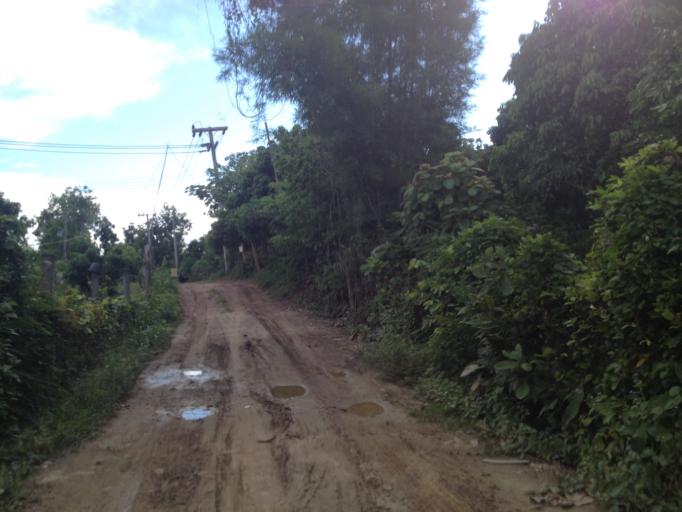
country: TH
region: Chiang Mai
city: Hang Dong
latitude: 18.7012
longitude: 98.8929
